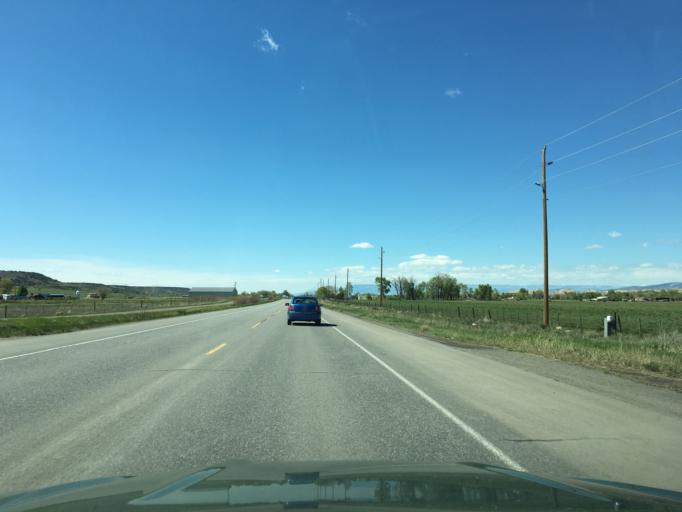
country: US
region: Colorado
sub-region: Montrose County
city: Montrose
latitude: 38.3525
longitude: -107.7966
